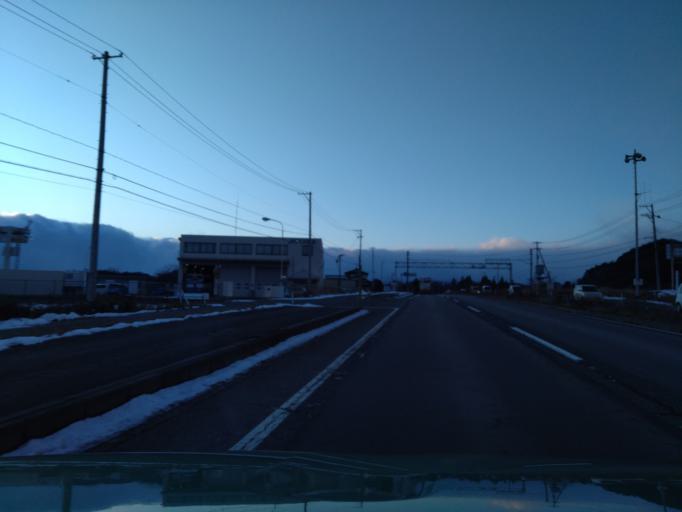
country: JP
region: Iwate
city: Shizukuishi
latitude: 39.7008
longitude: 141.0511
